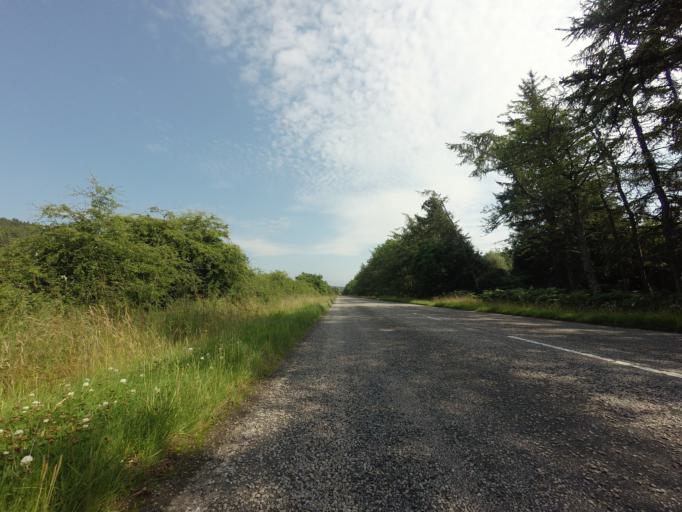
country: GB
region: Scotland
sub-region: Highland
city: Evanton
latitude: 57.9172
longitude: -4.3922
